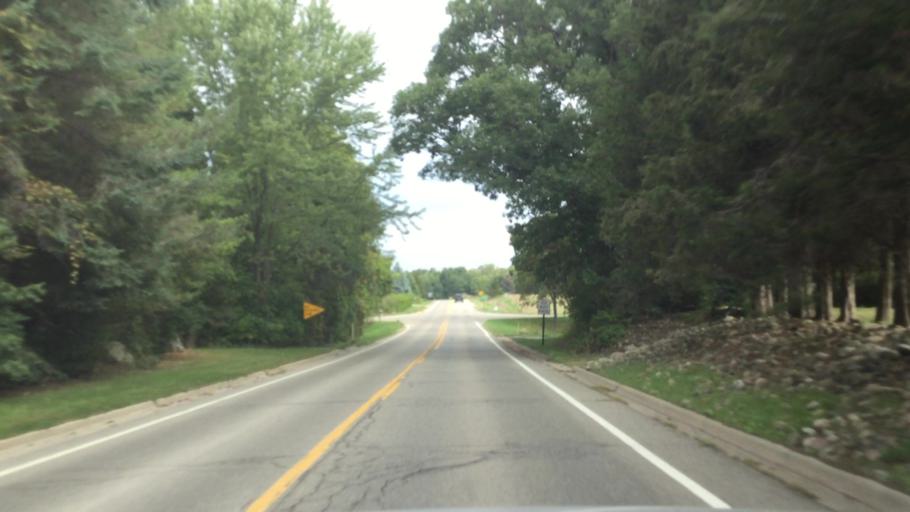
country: US
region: Michigan
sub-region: Livingston County
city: Howell
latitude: 42.6882
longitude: -83.8779
